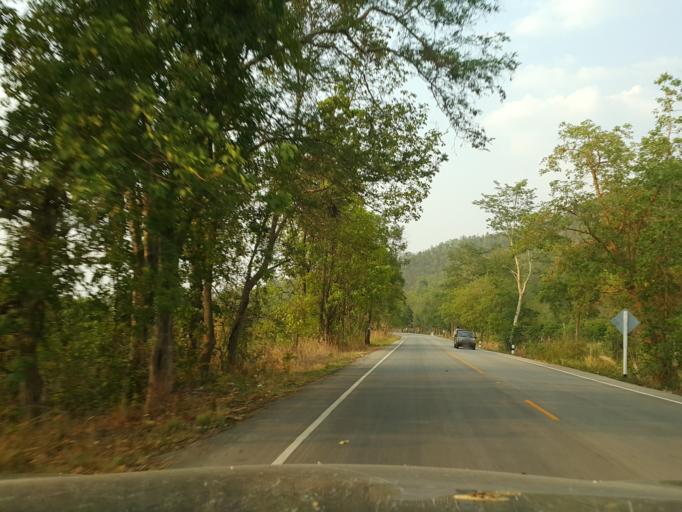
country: TH
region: Lamphun
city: Li
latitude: 17.8328
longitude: 98.9891
